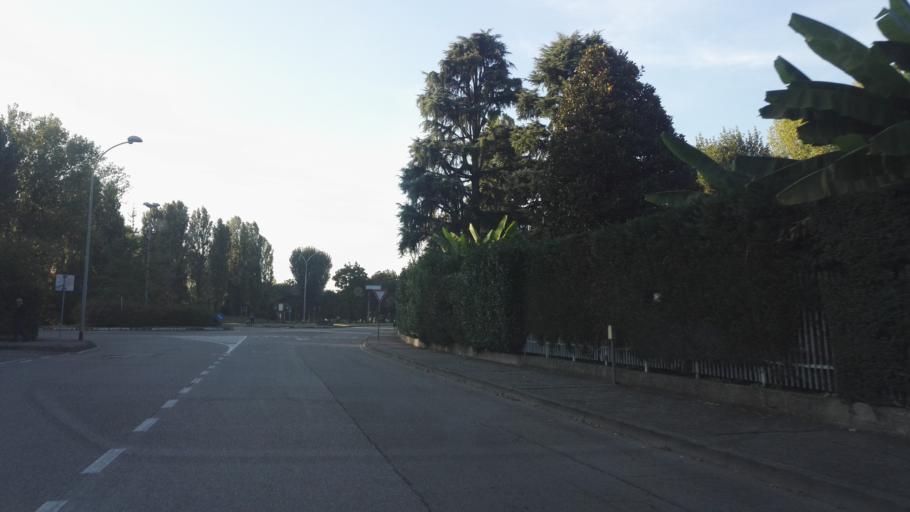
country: IT
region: Lombardy
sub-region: Citta metropolitana di Milano
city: San Bovio-San Felice
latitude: 45.4611
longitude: 9.3144
